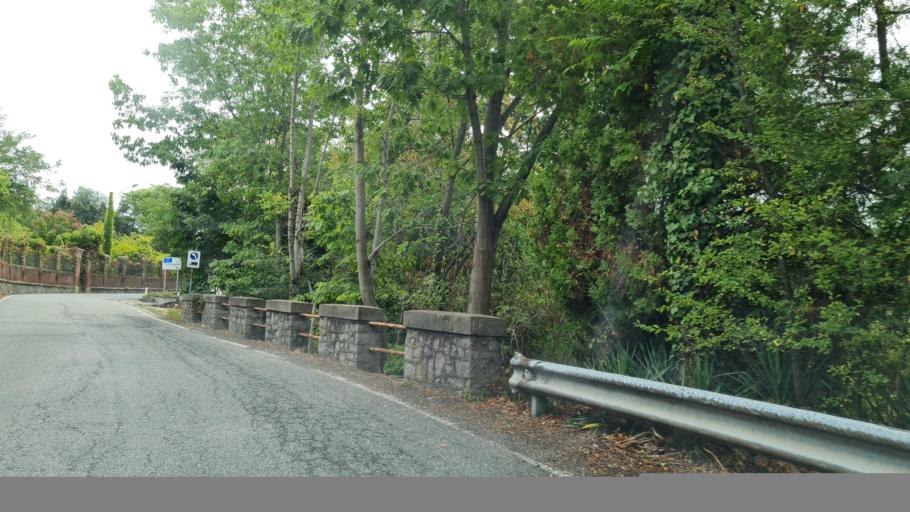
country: IT
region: Piedmont
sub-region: Provincia di Biella
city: Lessona
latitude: 45.5912
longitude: 8.1904
